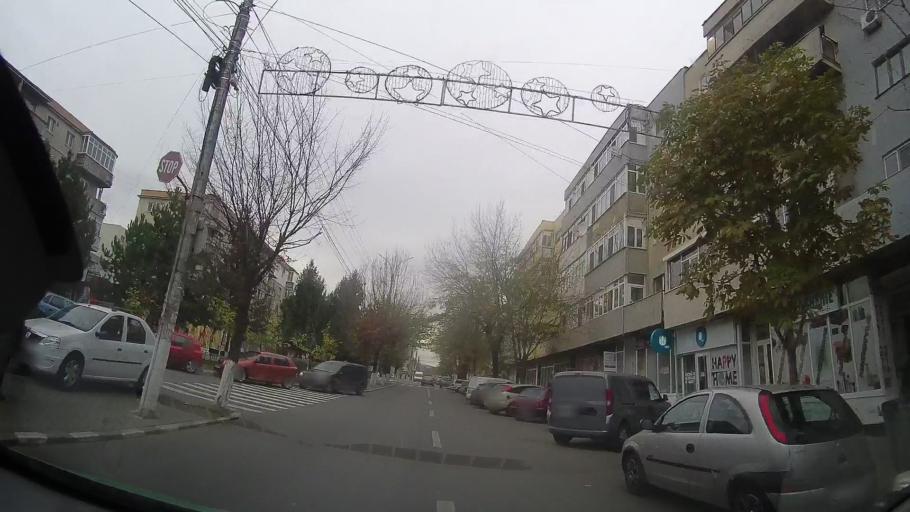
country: RO
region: Prahova
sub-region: Oras Urlati
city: Urlati
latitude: 44.9911
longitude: 26.2340
